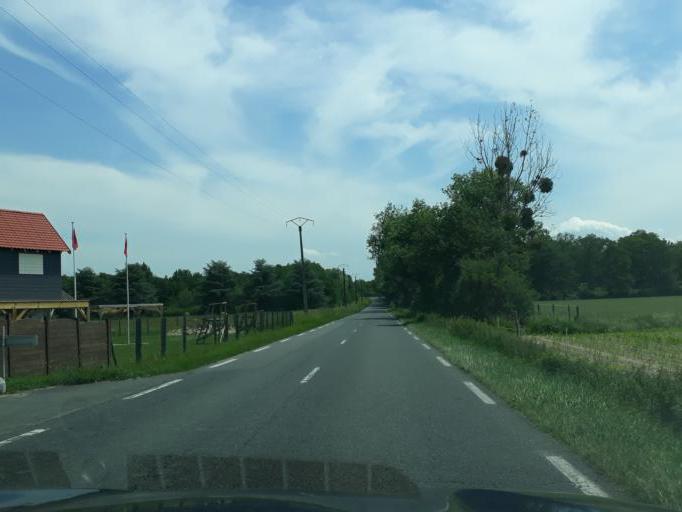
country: FR
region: Centre
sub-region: Departement du Loiret
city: Sandillon
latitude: 47.8063
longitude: 2.0659
